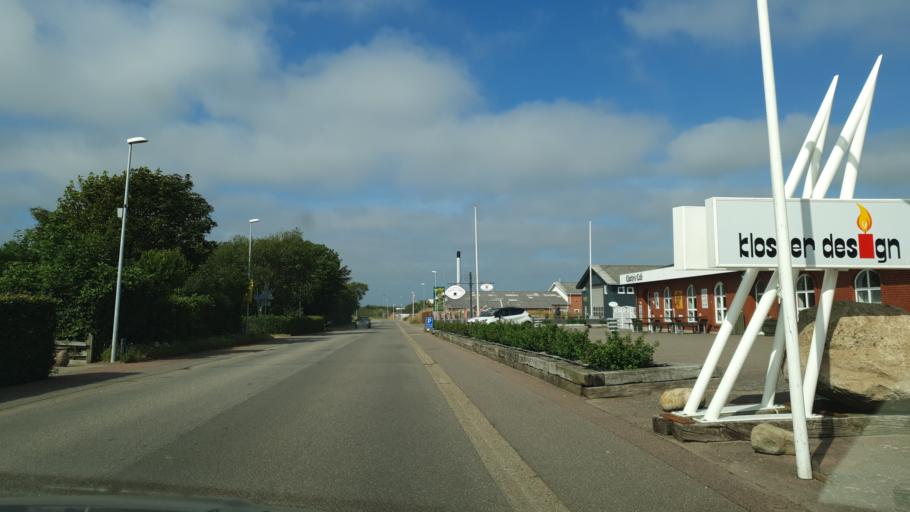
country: DK
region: Central Jutland
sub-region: Ringkobing-Skjern Kommune
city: Ringkobing
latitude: 56.1296
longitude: 8.1807
